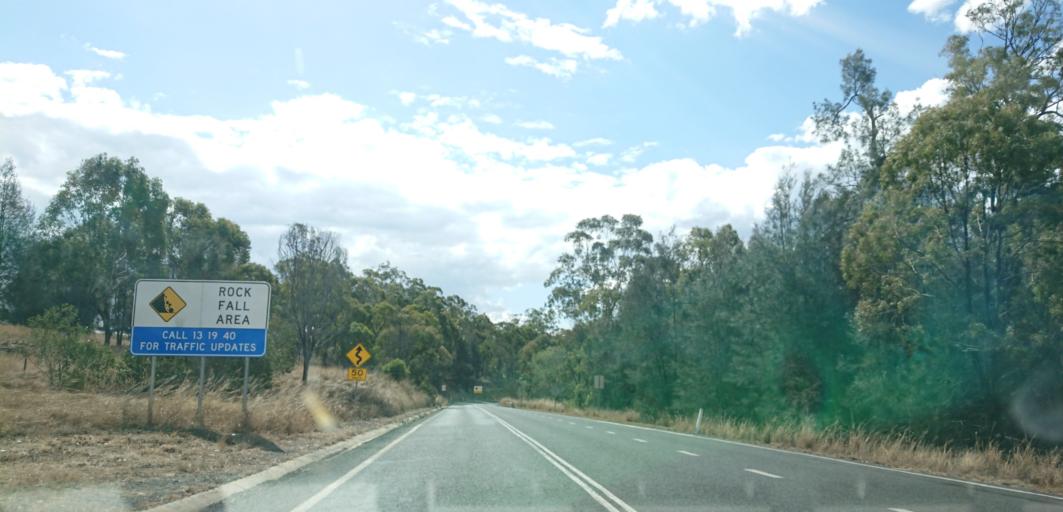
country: AU
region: Queensland
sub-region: Toowoomba
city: Top Camp
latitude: -27.7829
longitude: 152.0980
